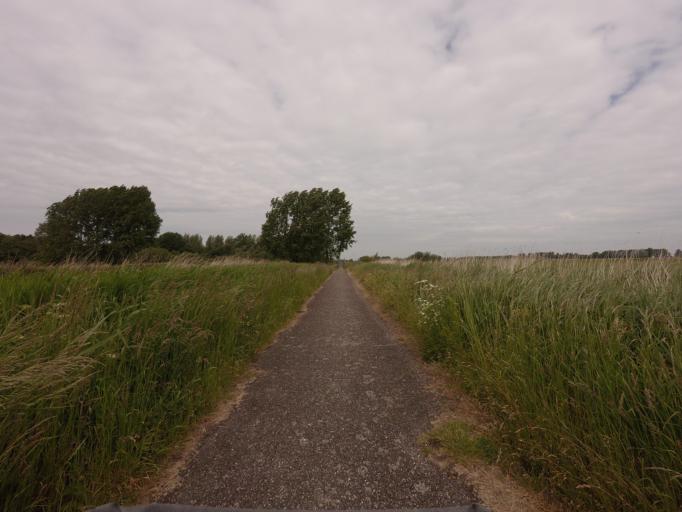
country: NL
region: North Holland
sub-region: Gemeente Medemblik
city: Medemblik
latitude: 52.7423
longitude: 5.1224
